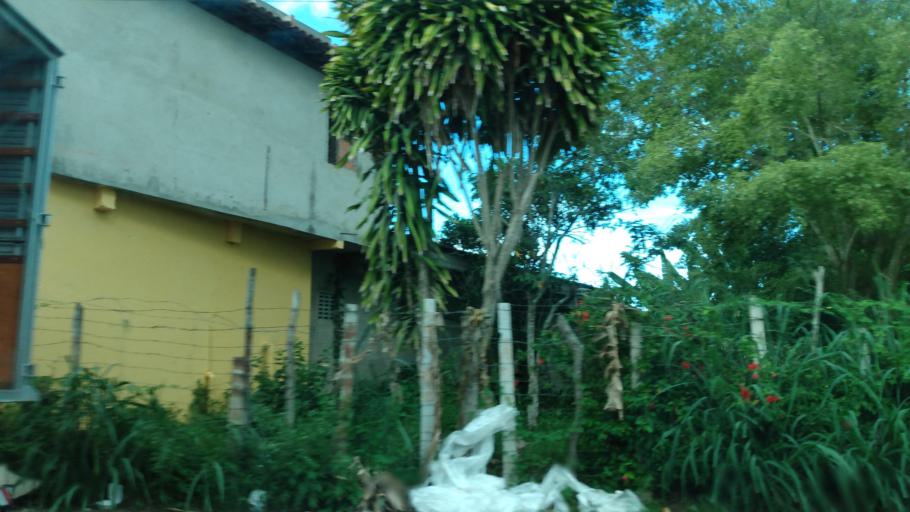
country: BR
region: Pernambuco
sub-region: Gravata
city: Gravata
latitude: -8.2010
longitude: -35.5681
